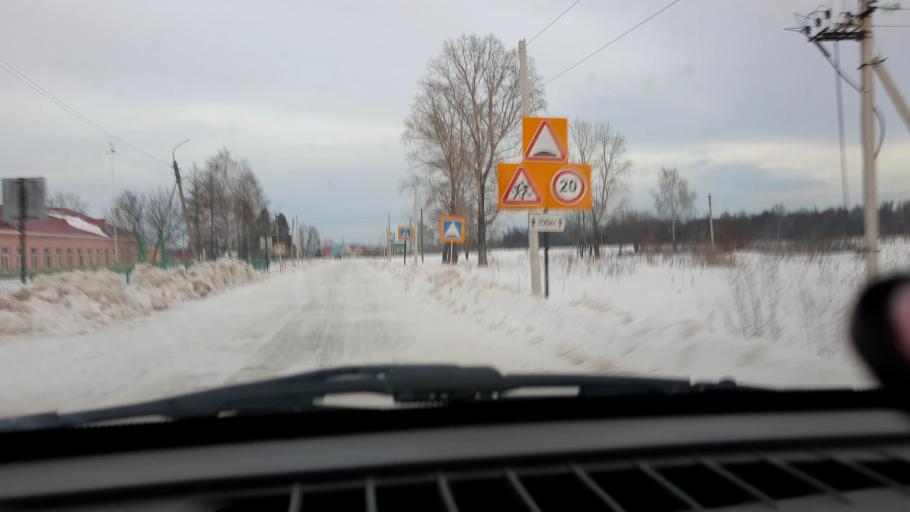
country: RU
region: Bashkortostan
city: Urman
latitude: 54.8662
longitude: 56.8599
